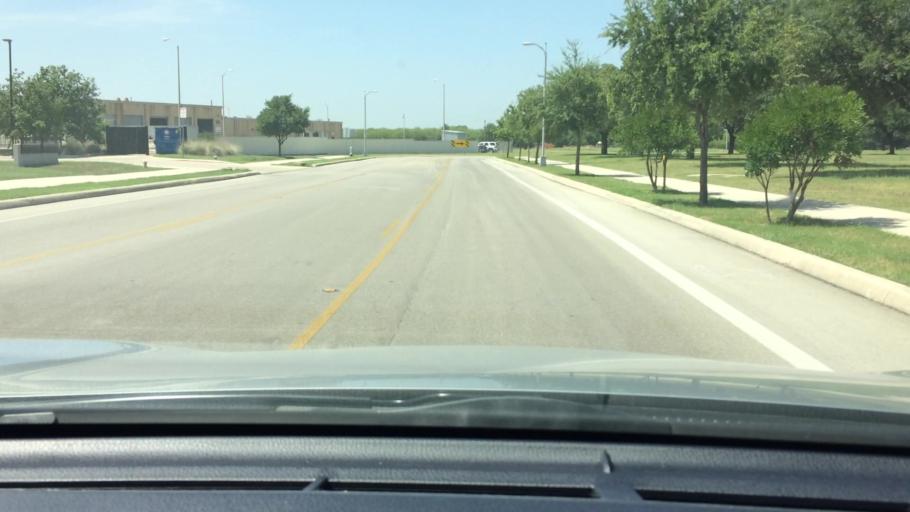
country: US
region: Texas
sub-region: Bexar County
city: San Antonio
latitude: 29.3422
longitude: -98.4448
